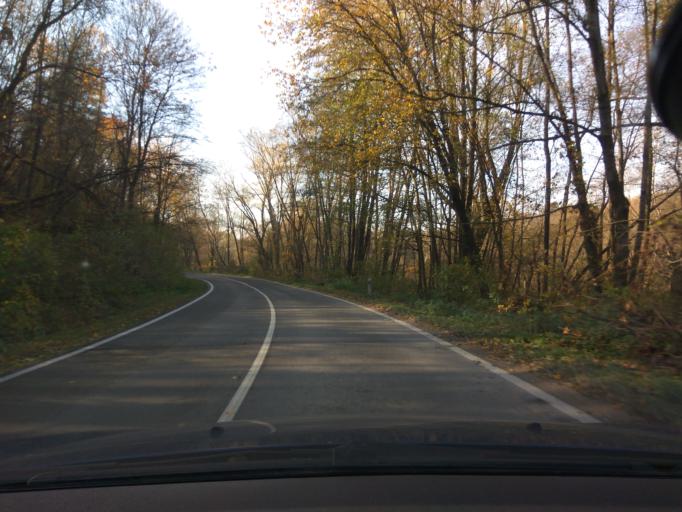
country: SK
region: Nitriansky
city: Brezova pod Bradlom
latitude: 48.6336
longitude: 17.4967
